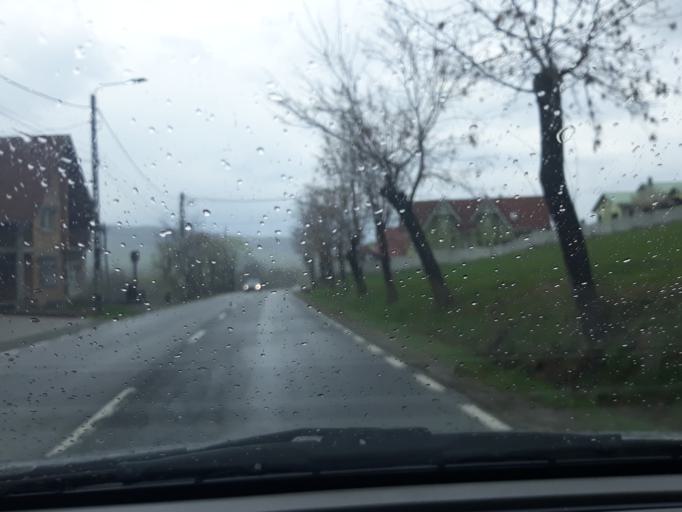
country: RO
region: Harghita
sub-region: Comuna Corund
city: Corund
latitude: 46.4791
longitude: 25.1740
